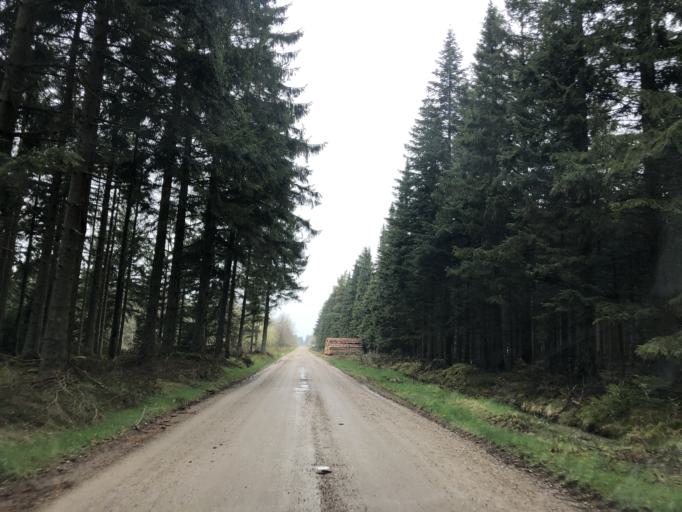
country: DK
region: Central Jutland
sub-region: Lemvig Kommune
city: Lemvig
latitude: 56.4905
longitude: 8.3504
